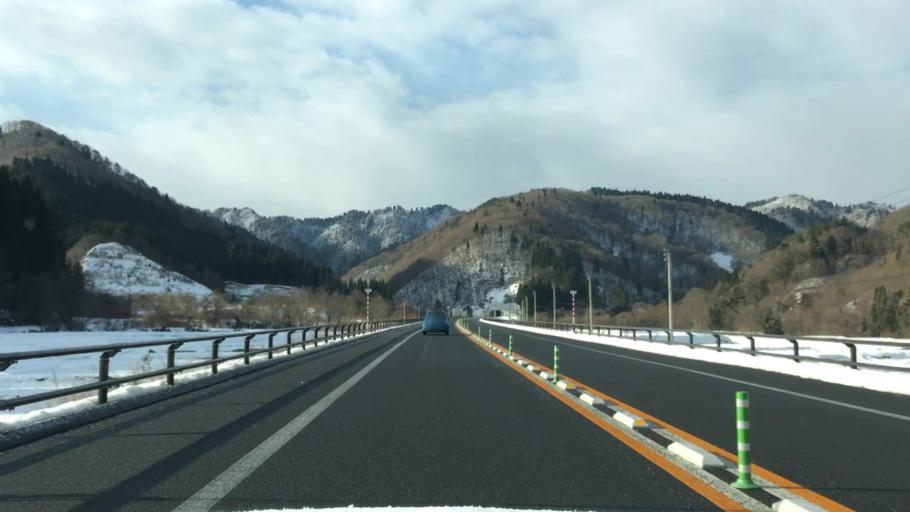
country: JP
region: Akita
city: Odate
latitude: 40.2335
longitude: 140.4956
